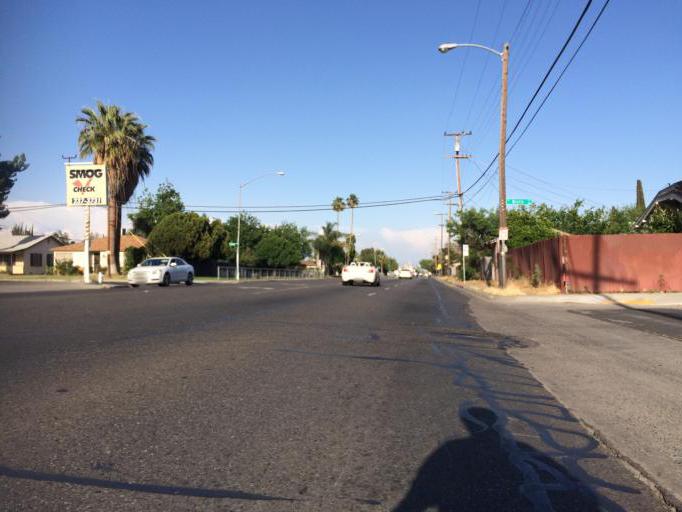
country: US
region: California
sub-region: Fresno County
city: Fresno
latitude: 36.7431
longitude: -119.7596
